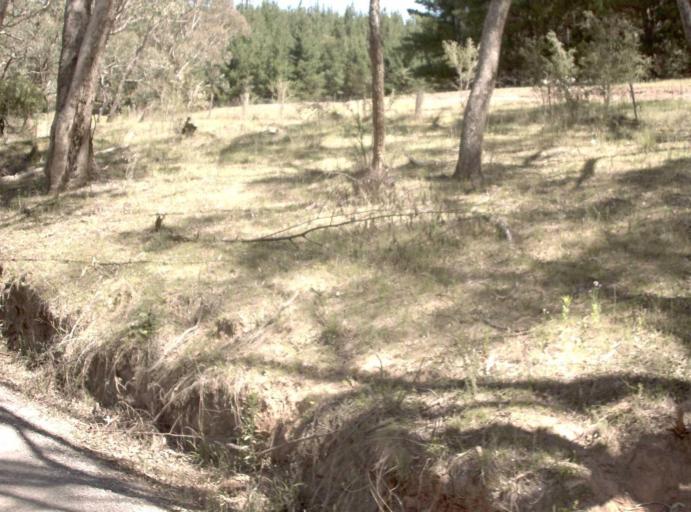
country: AU
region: New South Wales
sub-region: Bombala
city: Bombala
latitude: -37.1096
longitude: 148.6414
